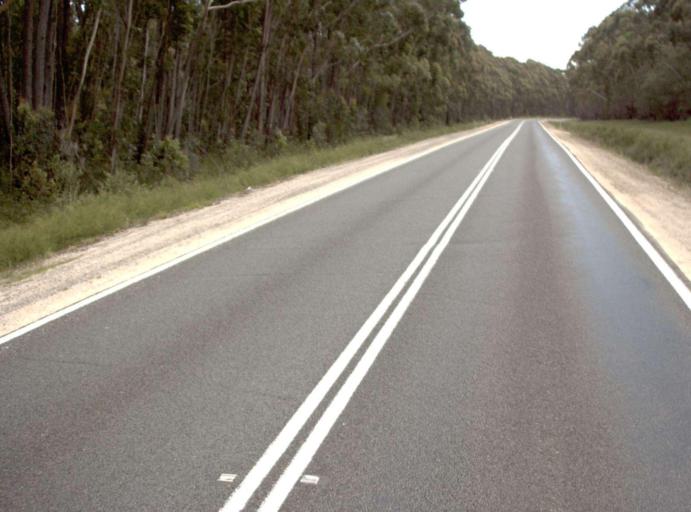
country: AU
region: New South Wales
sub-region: Bega Valley
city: Eden
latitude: -37.5361
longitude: 149.4768
